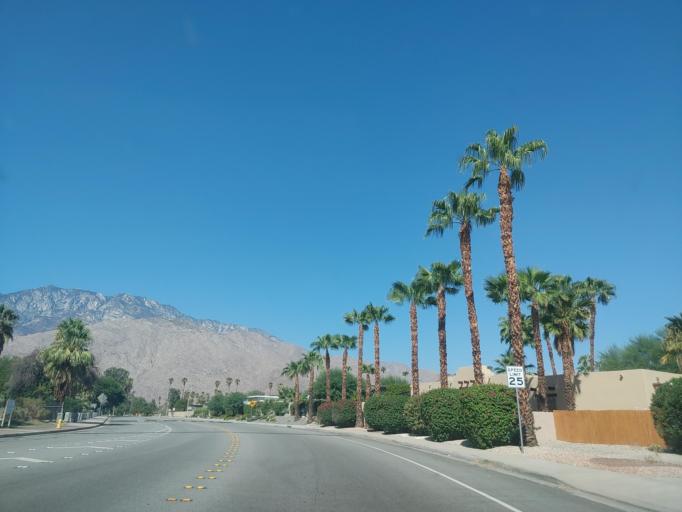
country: US
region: California
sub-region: Riverside County
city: Palm Springs
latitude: 33.8108
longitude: -116.5079
